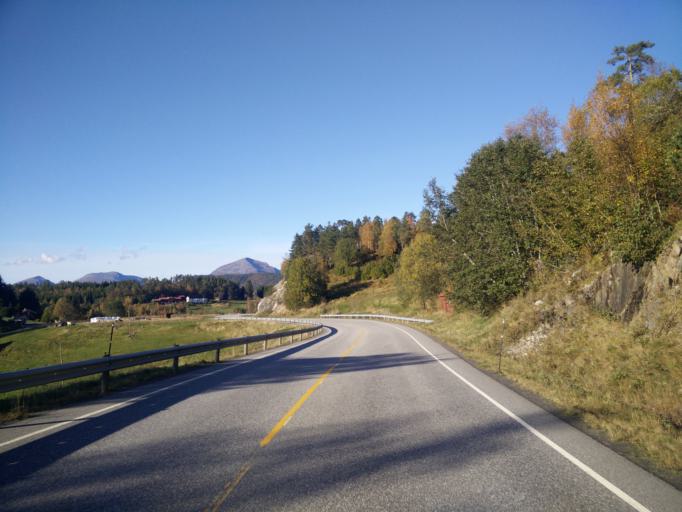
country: NO
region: More og Romsdal
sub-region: Halsa
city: Liaboen
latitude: 63.0967
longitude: 8.3456
